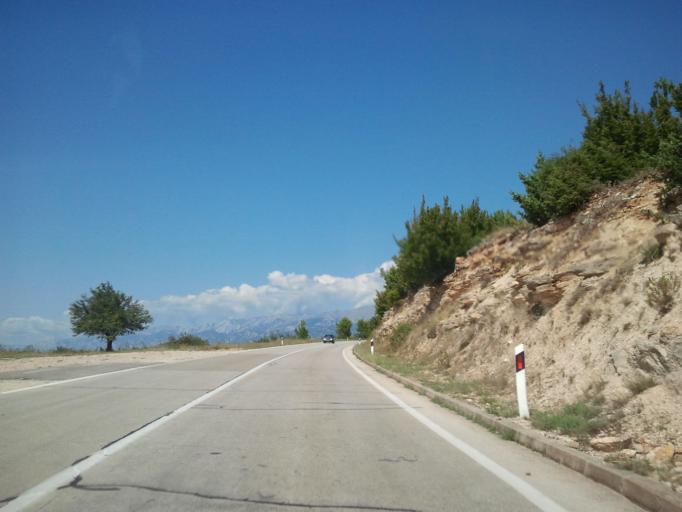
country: HR
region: Zadarska
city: Krusevo
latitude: 44.1562
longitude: 15.6256
